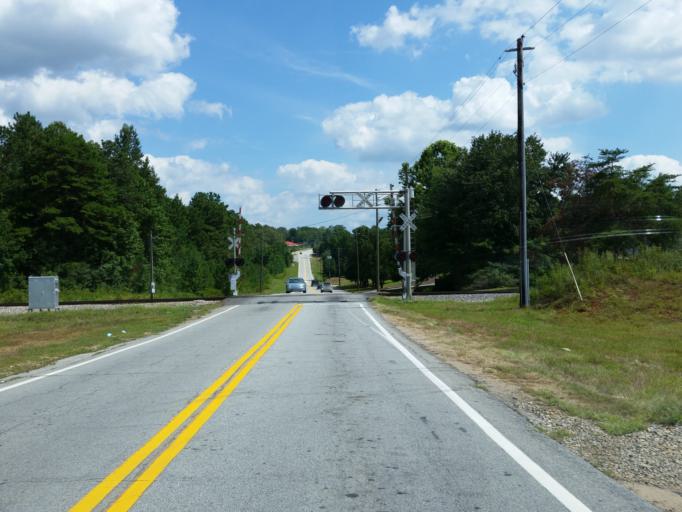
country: US
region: Georgia
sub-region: Gwinnett County
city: Lawrenceville
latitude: 33.9823
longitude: -83.9496
